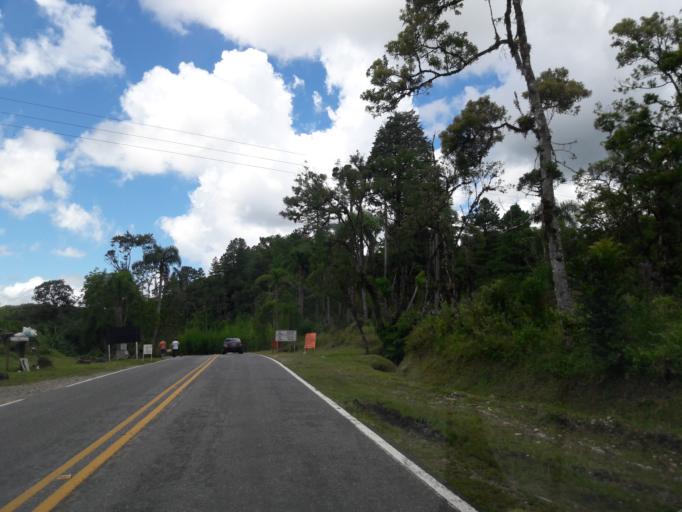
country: BR
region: Parana
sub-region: Campina Grande Do Sul
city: Campina Grande do Sul
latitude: -25.3085
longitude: -48.9423
